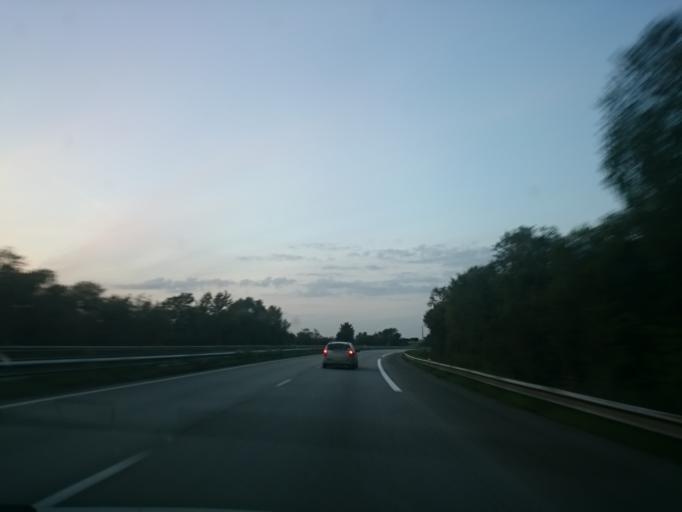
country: FR
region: Brittany
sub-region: Departement du Finistere
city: Chateaulin
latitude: 48.1841
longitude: -4.0470
